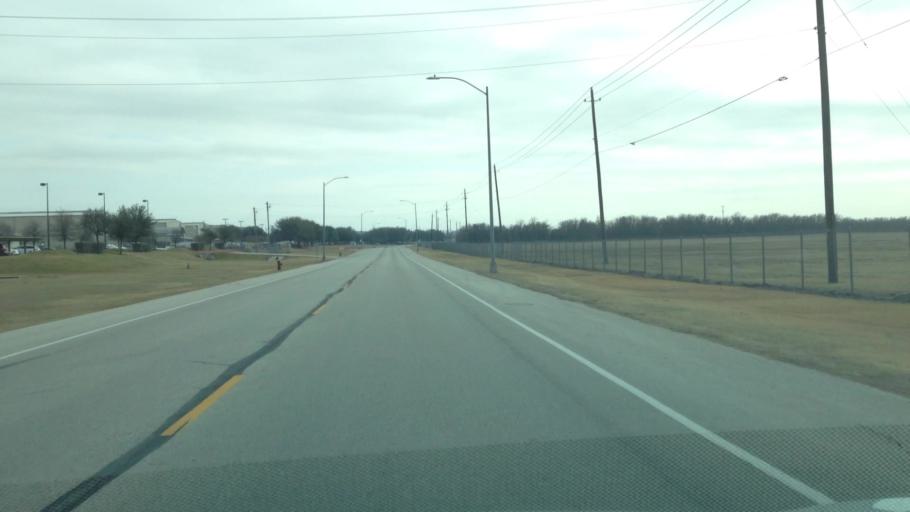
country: US
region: Texas
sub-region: Travis County
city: Hornsby Bend
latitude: 30.1909
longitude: -97.6637
